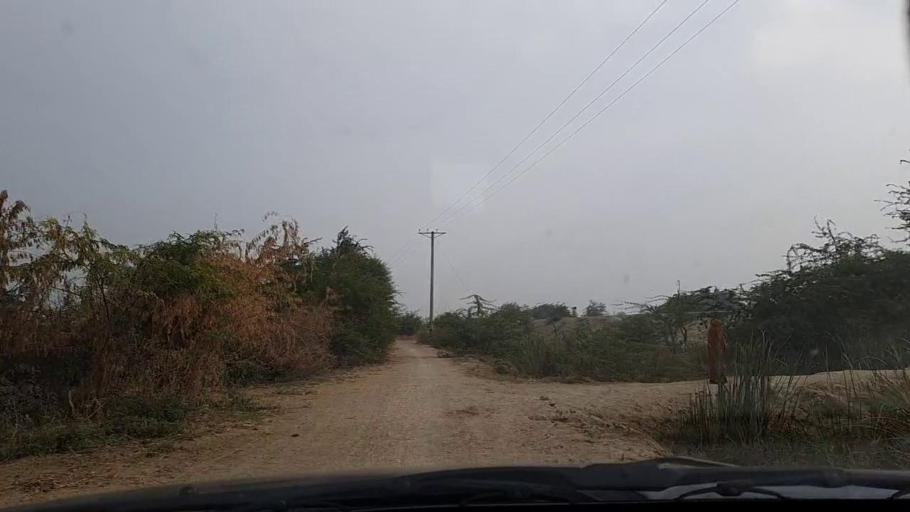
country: PK
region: Sindh
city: Tando Mittha Khan
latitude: 25.8038
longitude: 69.3804
